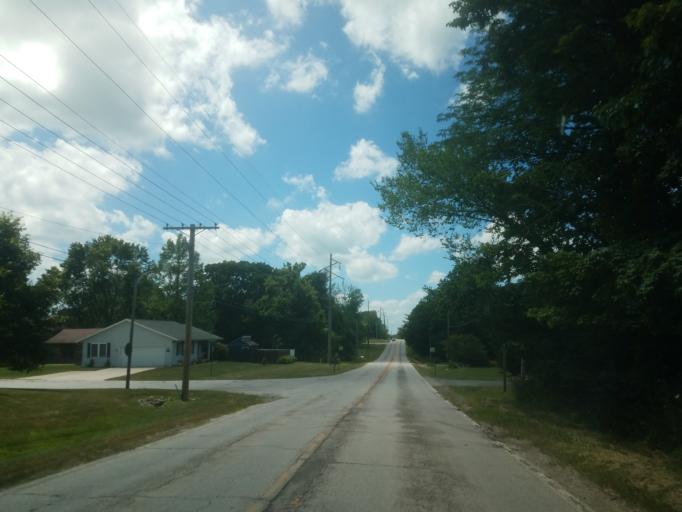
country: US
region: Illinois
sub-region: McLean County
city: Bloomington
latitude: 40.4589
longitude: -89.0154
